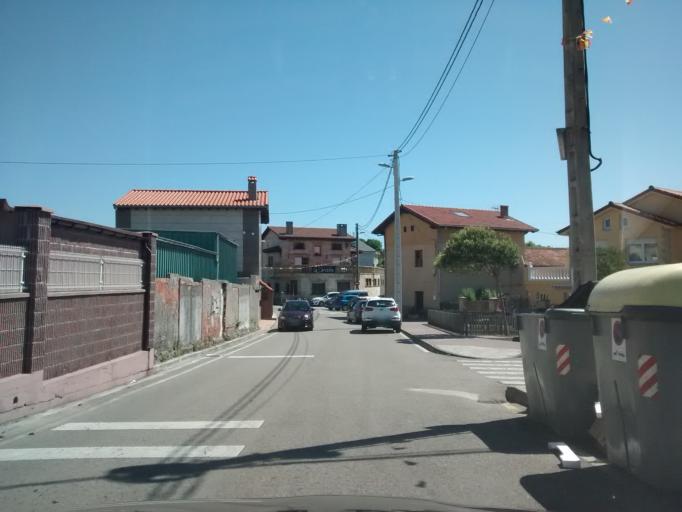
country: ES
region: Cantabria
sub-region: Provincia de Cantabria
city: Santander
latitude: 43.4713
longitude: -3.8305
